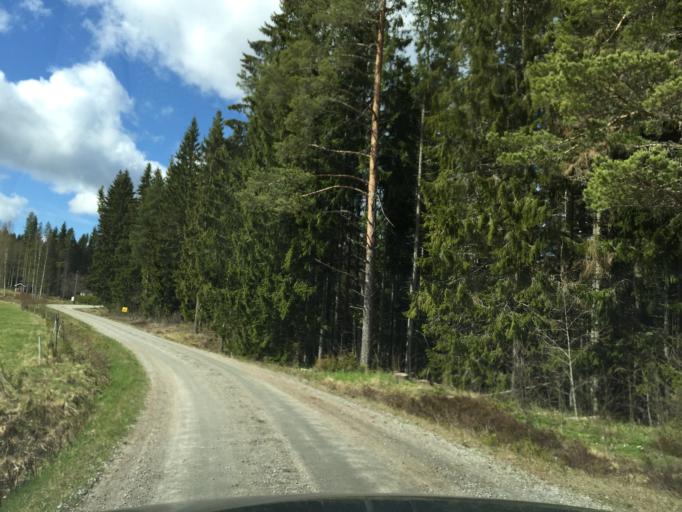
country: SE
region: Gaevleborg
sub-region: Bollnas Kommun
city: Arbra
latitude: 61.5232
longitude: 16.3217
